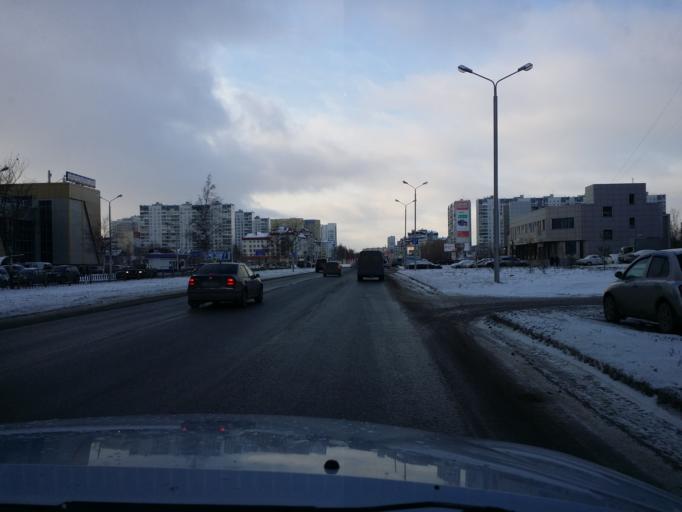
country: RU
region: Khanty-Mansiyskiy Avtonomnyy Okrug
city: Nizhnevartovsk
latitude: 60.9340
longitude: 76.5937
